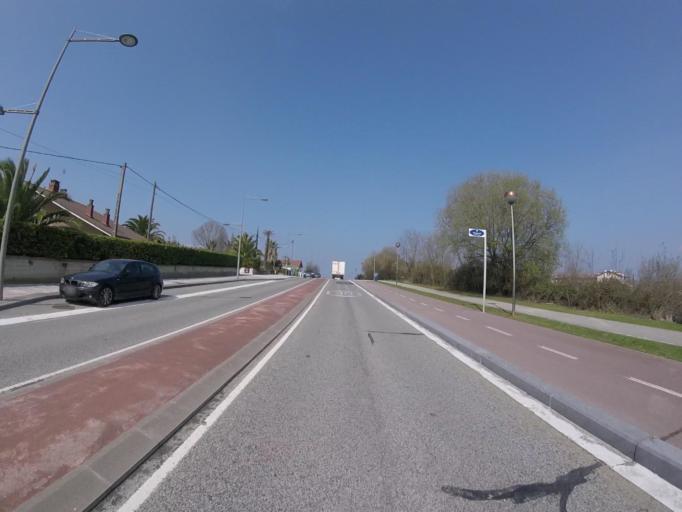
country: ES
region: Basque Country
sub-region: Provincia de Guipuzcoa
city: San Sebastian
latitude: 43.2931
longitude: -1.9912
